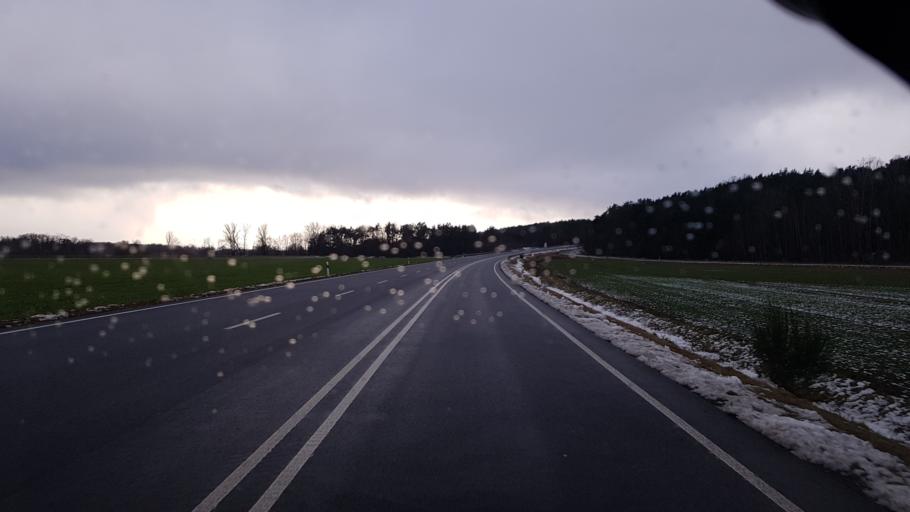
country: DE
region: Brandenburg
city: Schenkendobern
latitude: 51.8610
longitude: 14.6122
